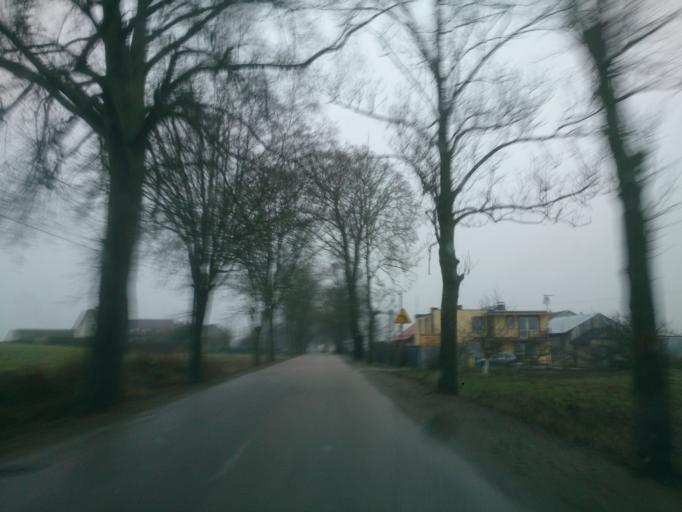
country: PL
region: Pomeranian Voivodeship
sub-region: Powiat koscierski
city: Stara Kiszewa
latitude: 53.9973
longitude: 18.1469
